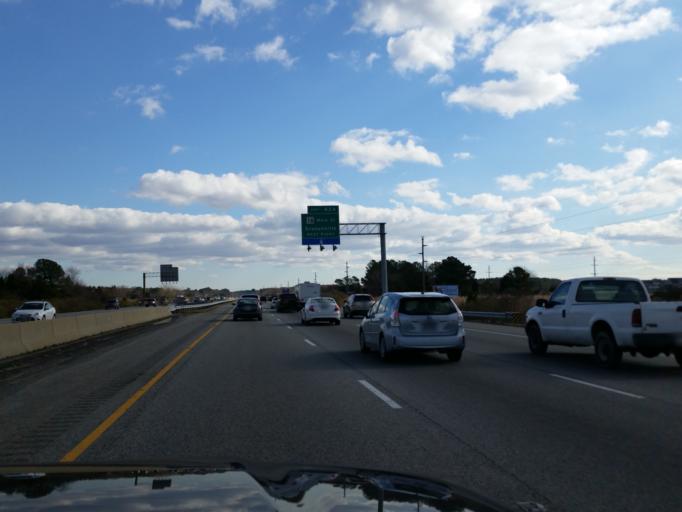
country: US
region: Maryland
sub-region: Queen Anne's County
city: Grasonville
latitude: 38.9673
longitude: -76.2329
